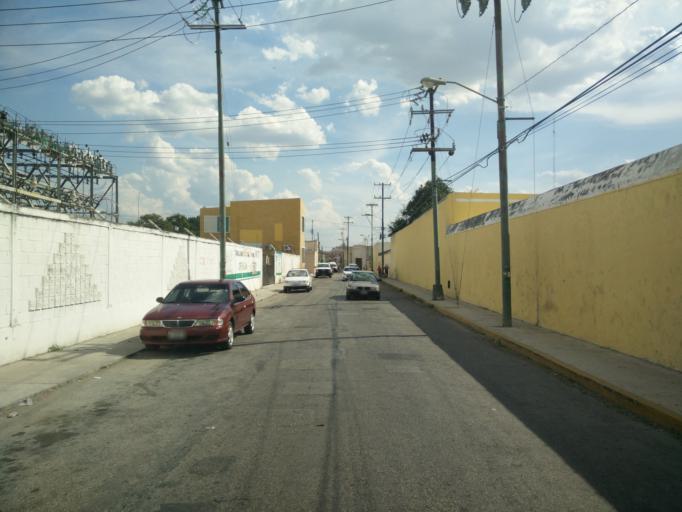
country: MX
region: Yucatan
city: Merida
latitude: 20.9672
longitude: -89.6150
